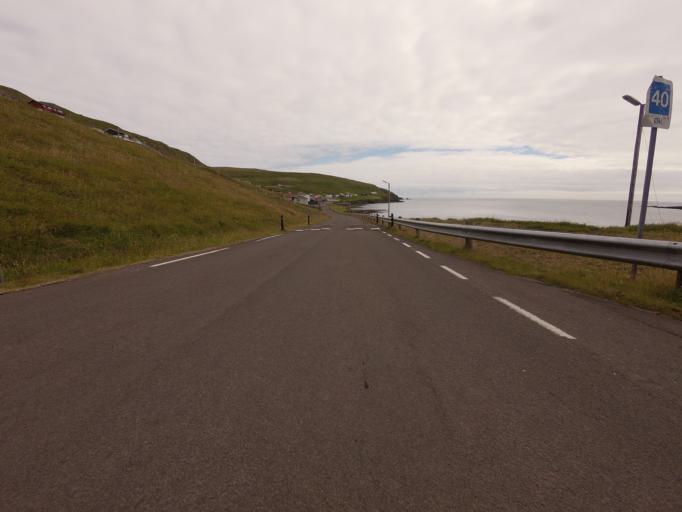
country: FO
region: Suduroy
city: Vagur
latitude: 61.4065
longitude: -6.7258
